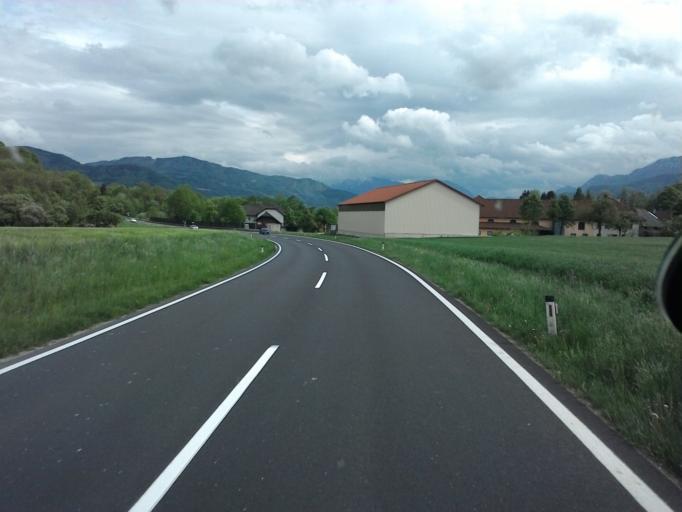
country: AT
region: Upper Austria
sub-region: Politischer Bezirk Kirchdorf an der Krems
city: Micheldorf in Oberoesterreich
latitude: 47.9251
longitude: 14.0902
